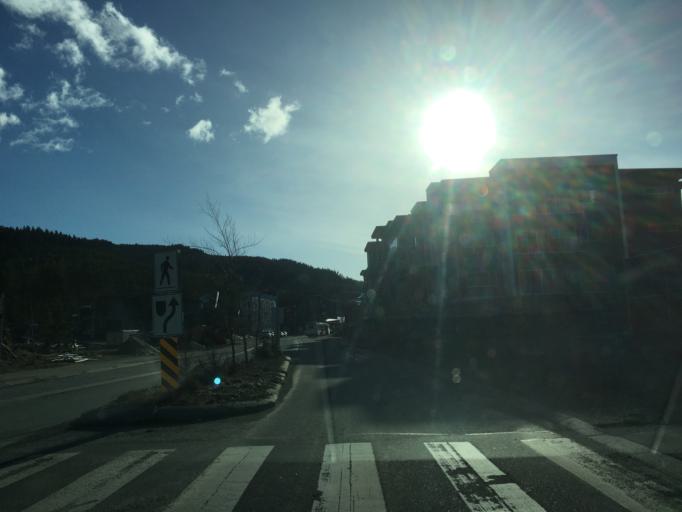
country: CA
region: British Columbia
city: Whistler
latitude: 50.0808
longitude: -123.0401
